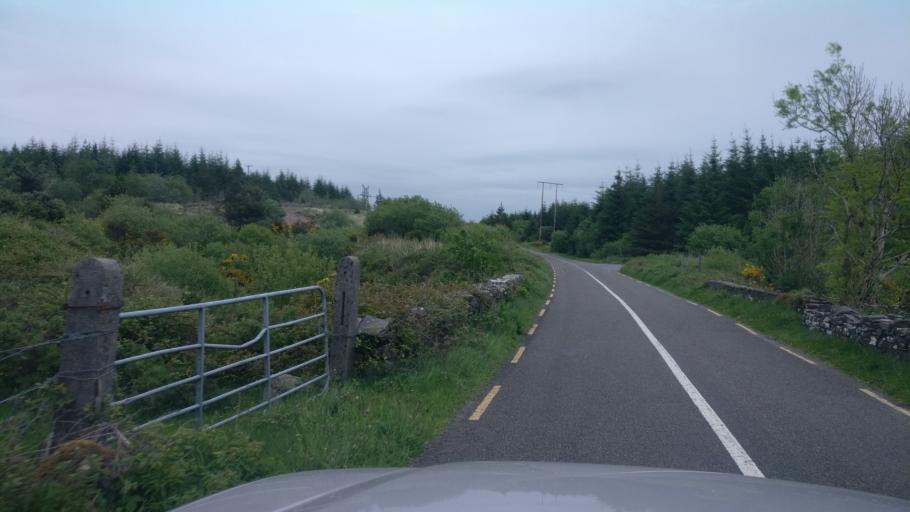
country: IE
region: Connaught
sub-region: County Galway
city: Loughrea
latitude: 53.0725
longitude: -8.5804
